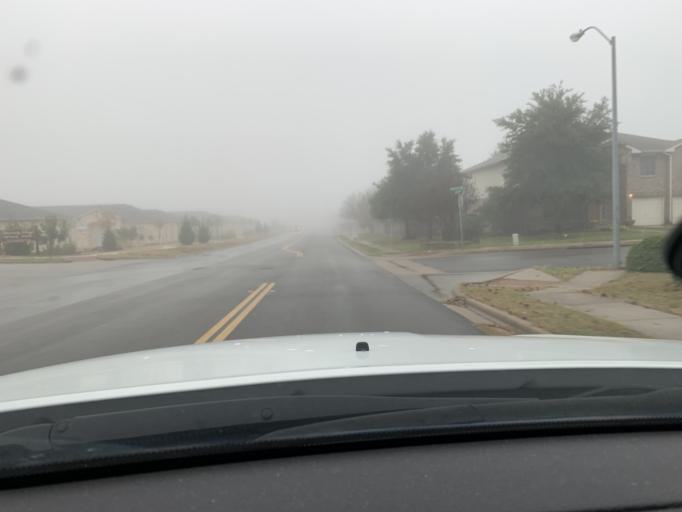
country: US
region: Texas
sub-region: Williamson County
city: Round Rock
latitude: 30.5658
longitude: -97.6643
